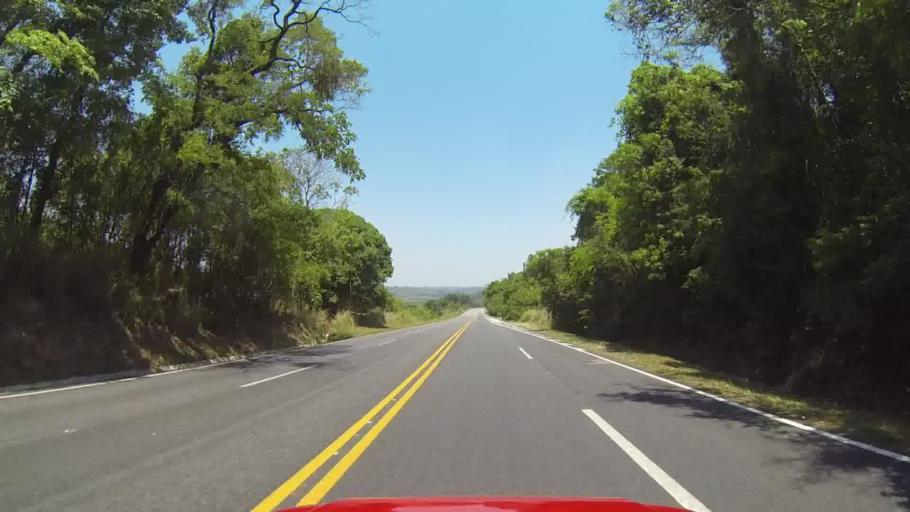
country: BR
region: Minas Gerais
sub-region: Itapecerica
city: Itapecerica
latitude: -20.2920
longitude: -45.1577
